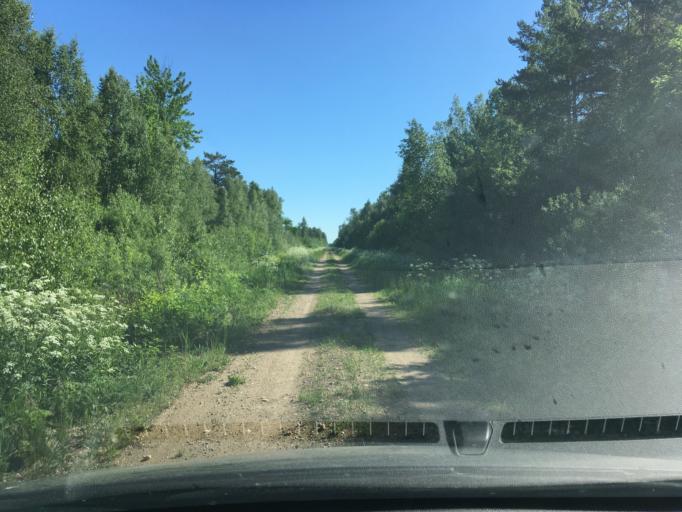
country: EE
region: Laeaene
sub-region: Lihula vald
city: Lihula
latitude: 58.6330
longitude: 23.7466
